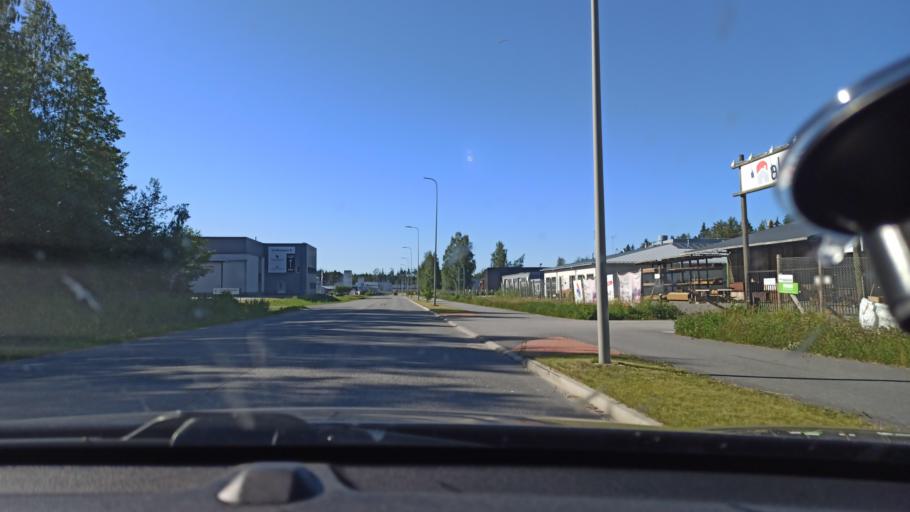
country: FI
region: Ostrobothnia
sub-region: Jakobstadsregionen
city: Jakobstad
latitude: 63.6856
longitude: 22.7107
